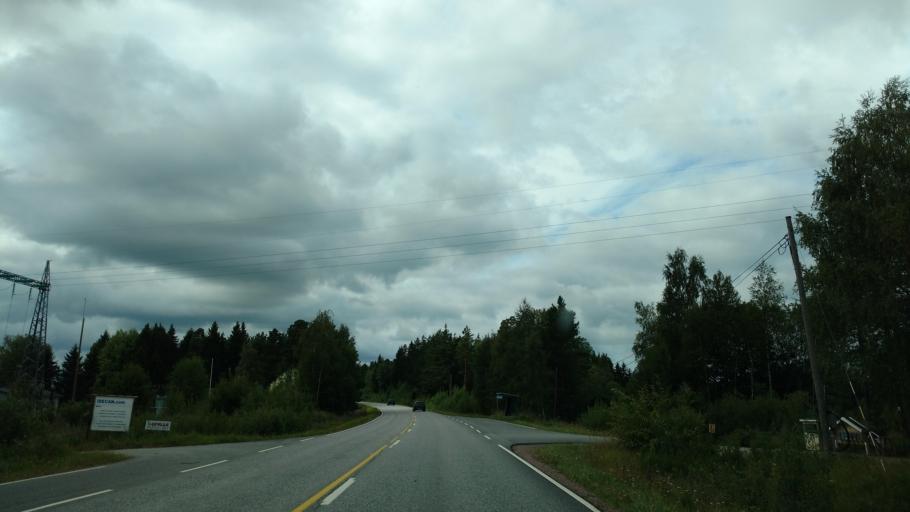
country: FI
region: Varsinais-Suomi
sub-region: Aboland-Turunmaa
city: Kimito
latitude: 60.1337
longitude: 22.6533
